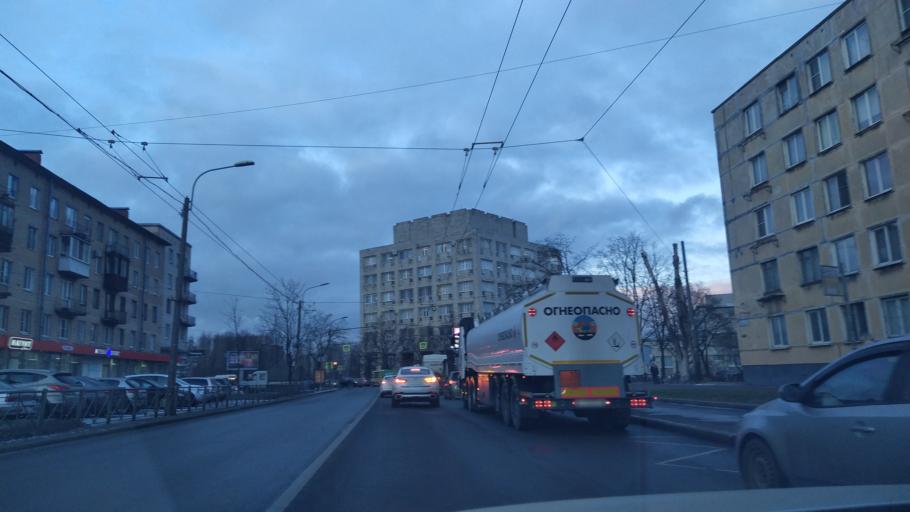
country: RU
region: St.-Petersburg
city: Dachnoye
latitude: 59.8563
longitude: 30.2564
